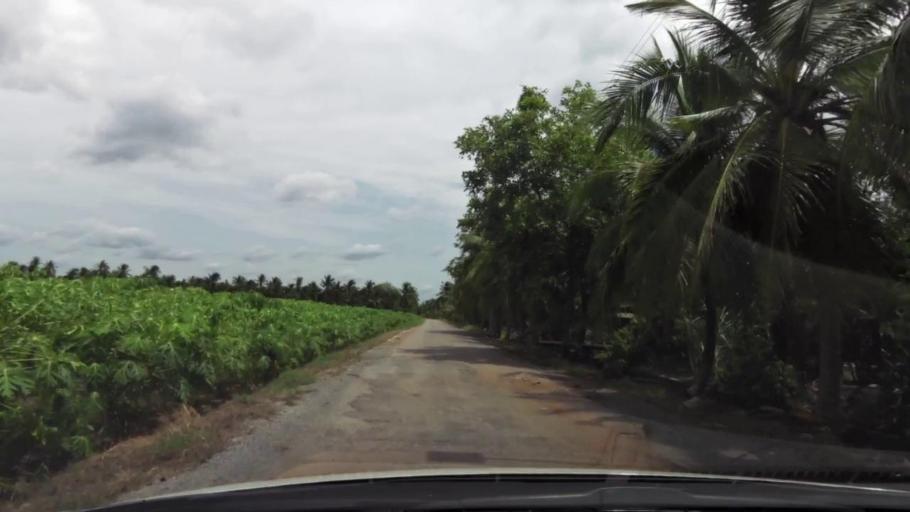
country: TH
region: Ratchaburi
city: Damnoen Saduak
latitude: 13.5318
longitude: 100.0013
